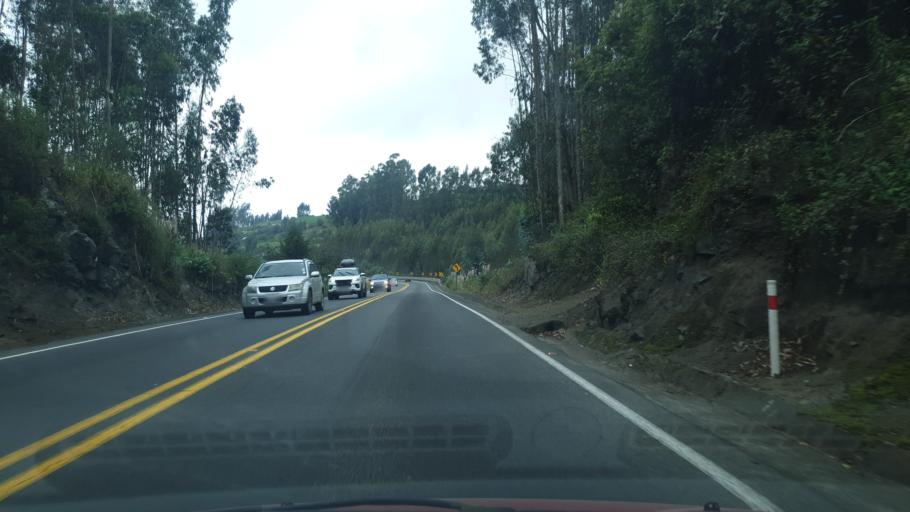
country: EC
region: Tungurahua
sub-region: Canton Quero
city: Quero
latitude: -1.3769
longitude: -78.6504
